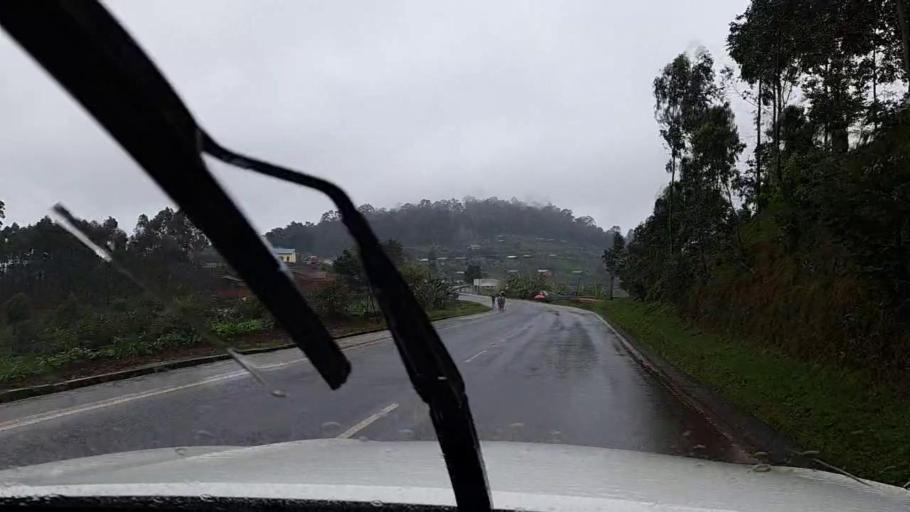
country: RW
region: Western Province
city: Cyangugu
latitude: -2.4630
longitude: 28.9989
